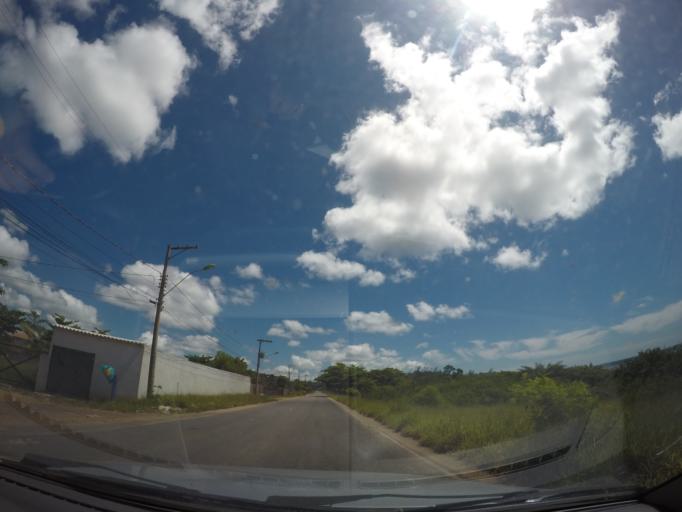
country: BR
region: Espirito Santo
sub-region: Serra
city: Serra
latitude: -20.0143
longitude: -40.1577
